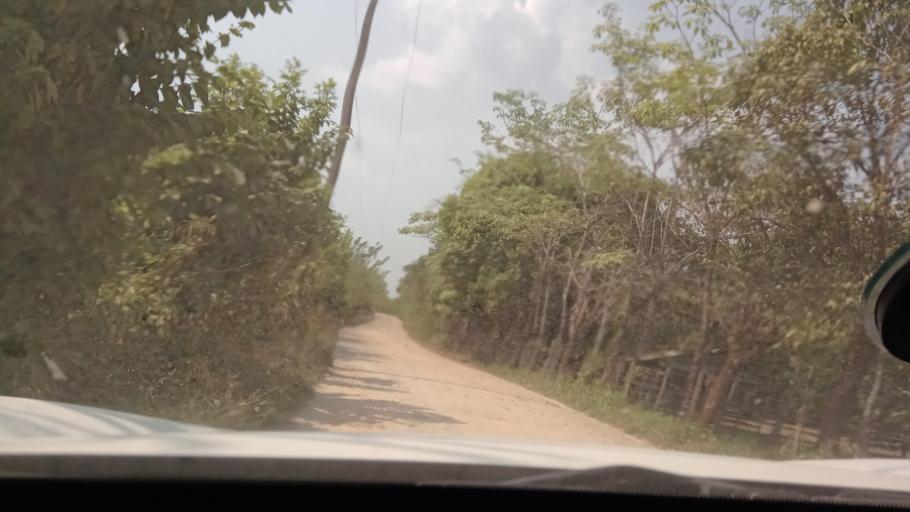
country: MX
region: Tabasco
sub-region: Huimanguillo
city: Francisco Rueda
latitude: 17.6794
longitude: -93.8621
